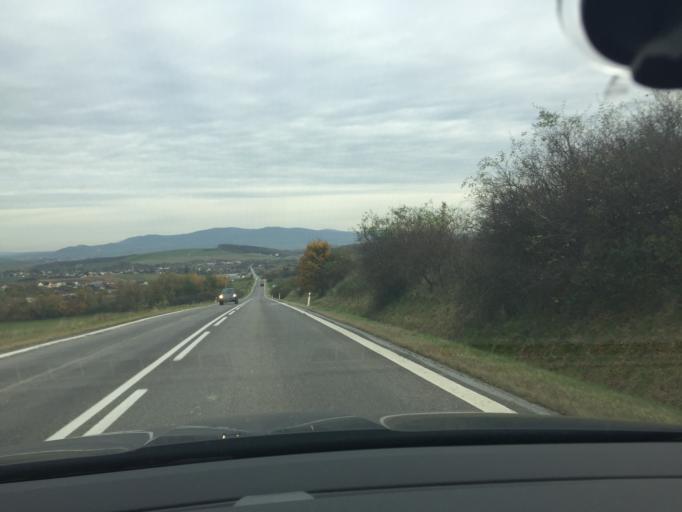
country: SK
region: Presovsky
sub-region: Okres Presov
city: Presov
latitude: 49.0074
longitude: 21.1497
